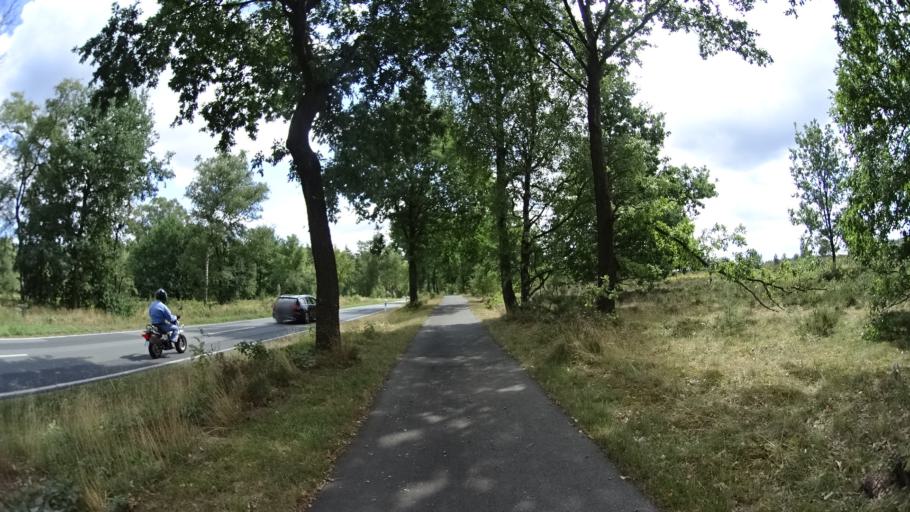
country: DE
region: Lower Saxony
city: Undeloh
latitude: 53.2138
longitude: 9.9493
